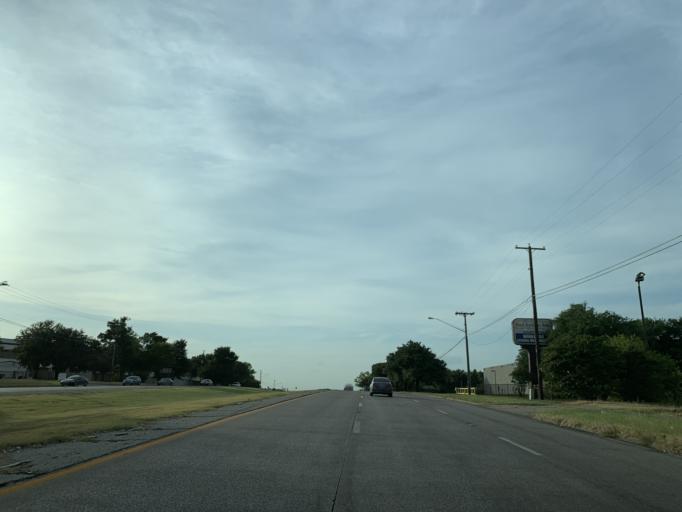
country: US
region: Texas
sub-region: Dallas County
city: Cockrell Hill
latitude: 32.6953
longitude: -96.8944
